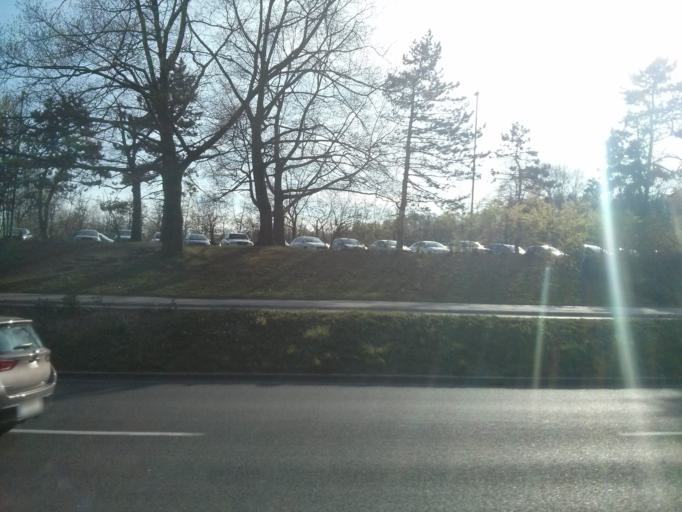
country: SI
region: Ljubljana
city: Ljubljana
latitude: 46.0582
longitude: 14.4998
